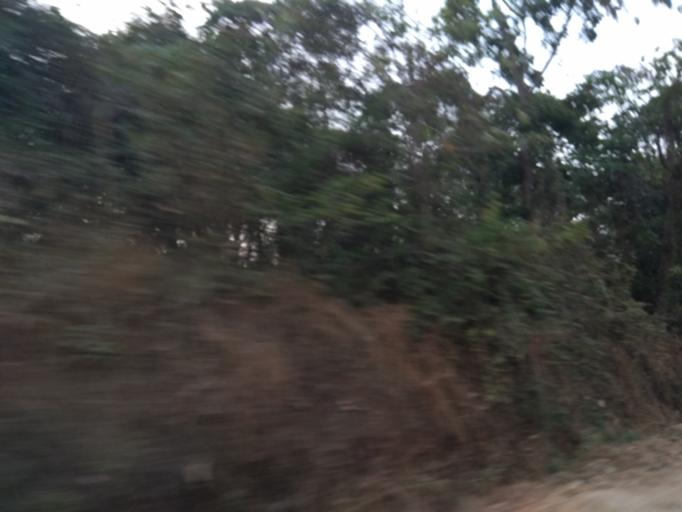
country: IN
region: Karnataka
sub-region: Dakshina Kannada
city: Mangalore
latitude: 12.9286
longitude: 74.8726
